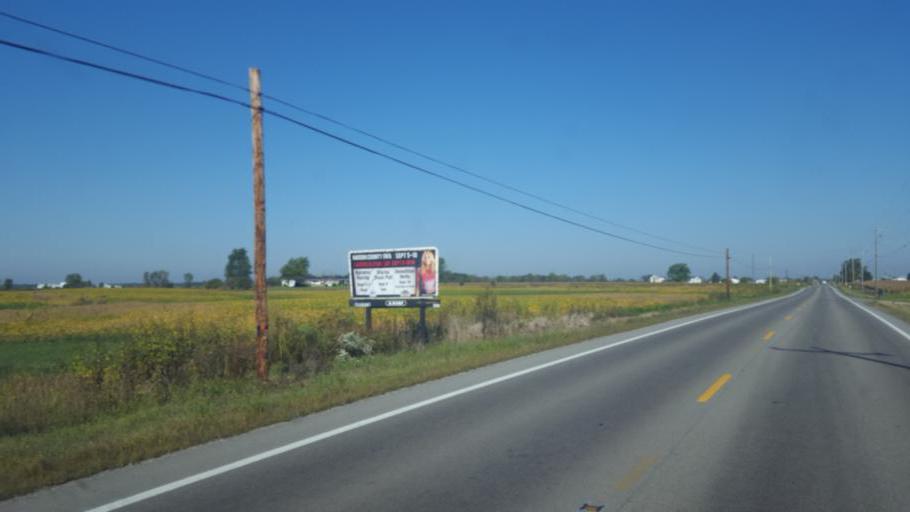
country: US
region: Ohio
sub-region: Hardin County
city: Kenton
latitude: 40.6011
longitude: -83.5752
